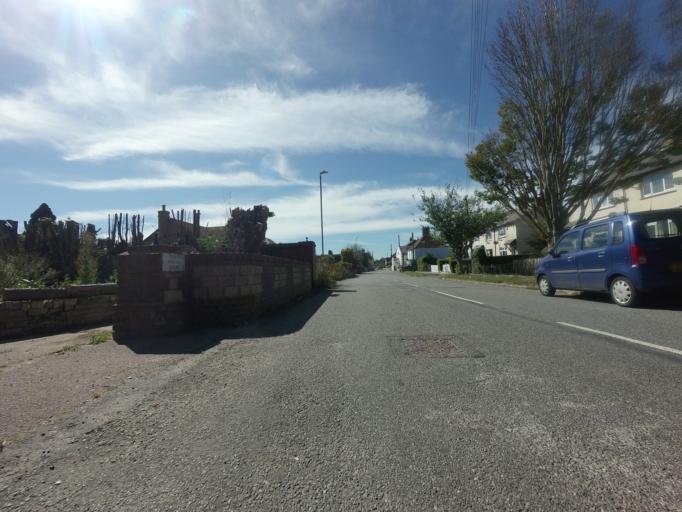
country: GB
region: England
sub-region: Kent
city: Birchington-on-Sea
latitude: 51.3383
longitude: 1.2830
